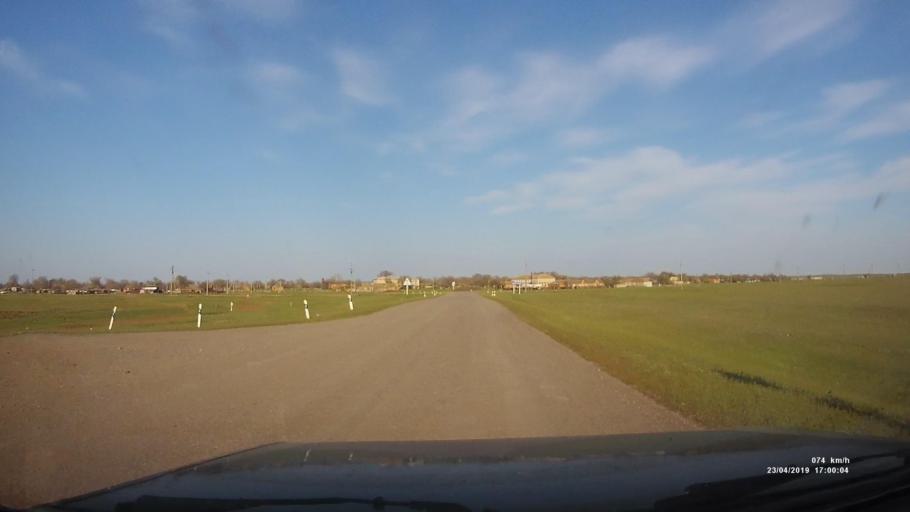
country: RU
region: Kalmykiya
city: Priyutnoye
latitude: 46.3083
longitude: 43.4012
